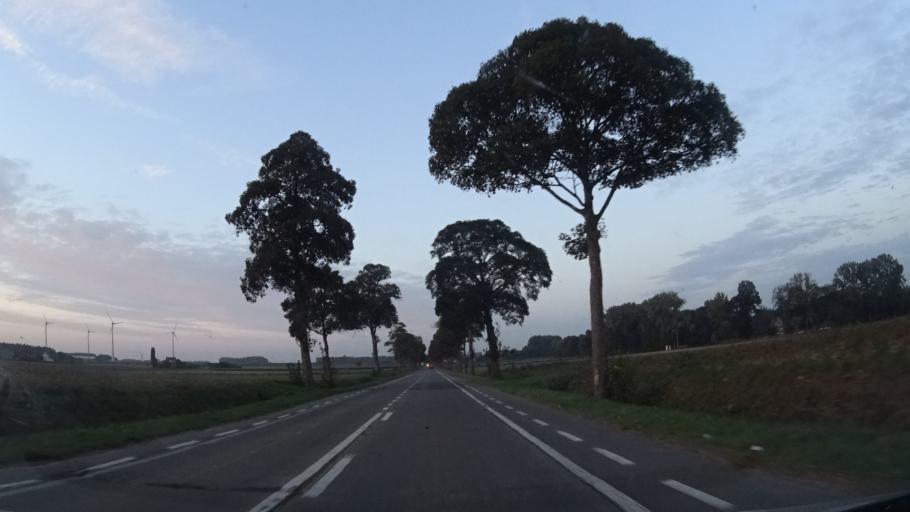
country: BE
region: Wallonia
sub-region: Province du Hainaut
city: Peruwelz
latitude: 50.5730
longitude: 3.6163
